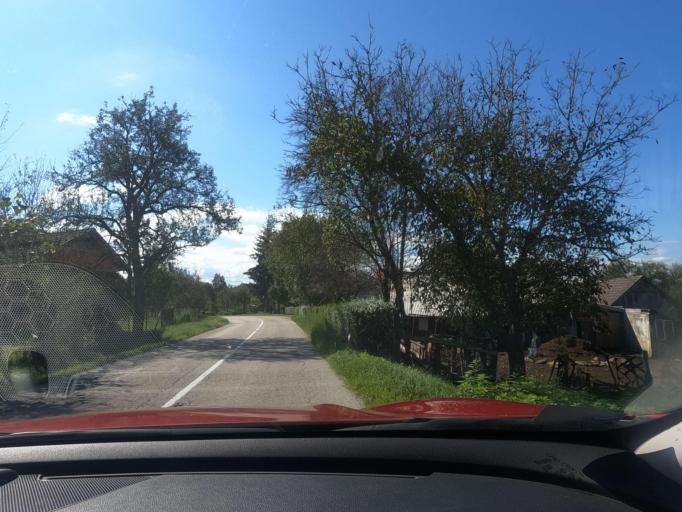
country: BA
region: Federation of Bosnia and Herzegovina
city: Vrnograc
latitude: 45.2607
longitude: 15.9498
